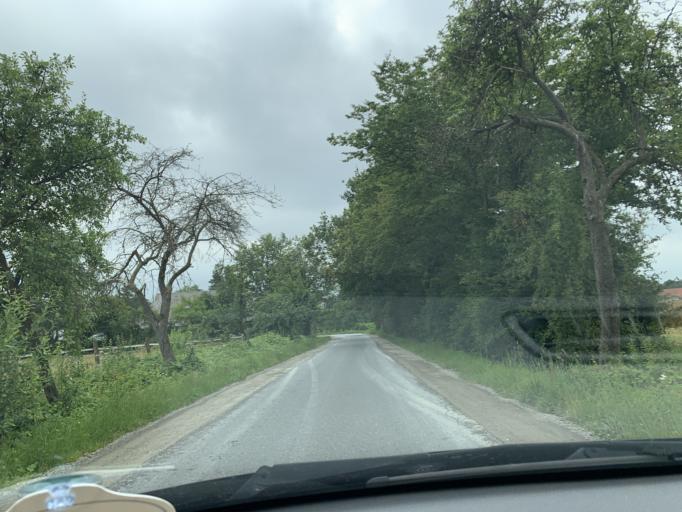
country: DE
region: North Rhine-Westphalia
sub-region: Regierungsbezirk Munster
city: Ennigerloh
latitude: 51.8329
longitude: 8.0731
